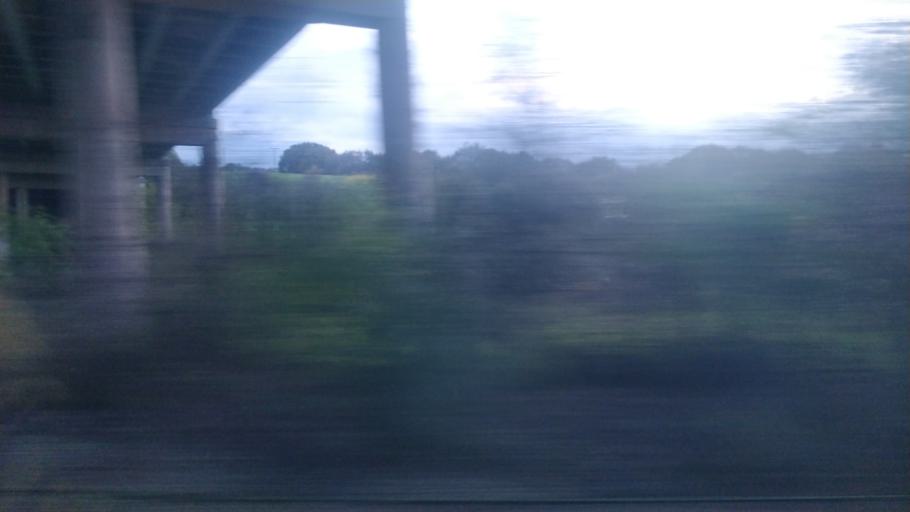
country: GB
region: England
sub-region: Borough of Wigan
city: Shevington
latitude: 53.5616
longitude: -2.7012
